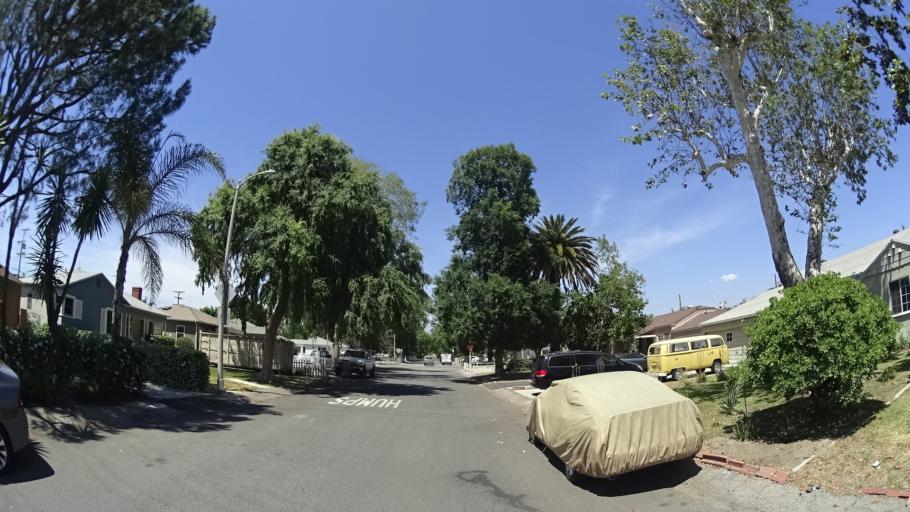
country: US
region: California
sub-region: Los Angeles County
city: North Hollywood
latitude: 34.1842
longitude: -118.3813
